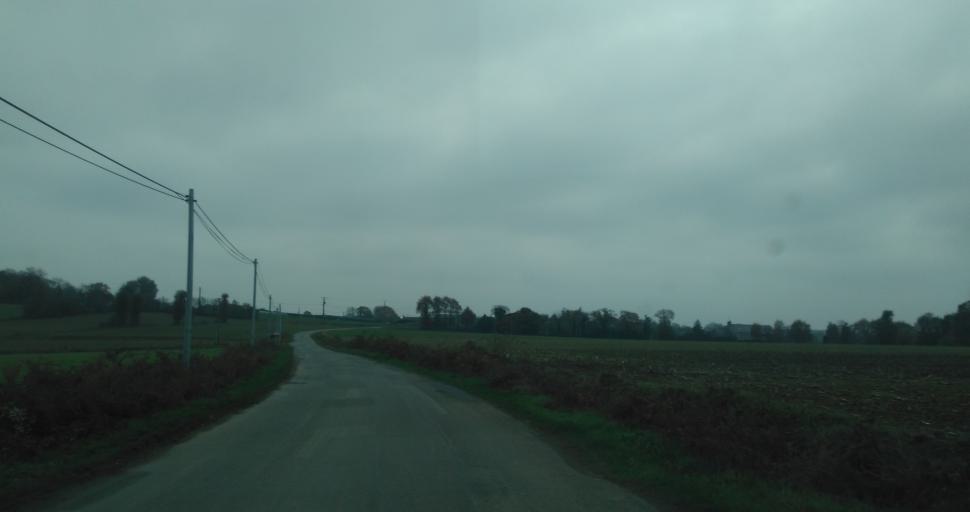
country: FR
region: Brittany
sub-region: Departement d'Ille-et-Vilaine
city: Iffendic
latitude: 48.0943
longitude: -2.0643
